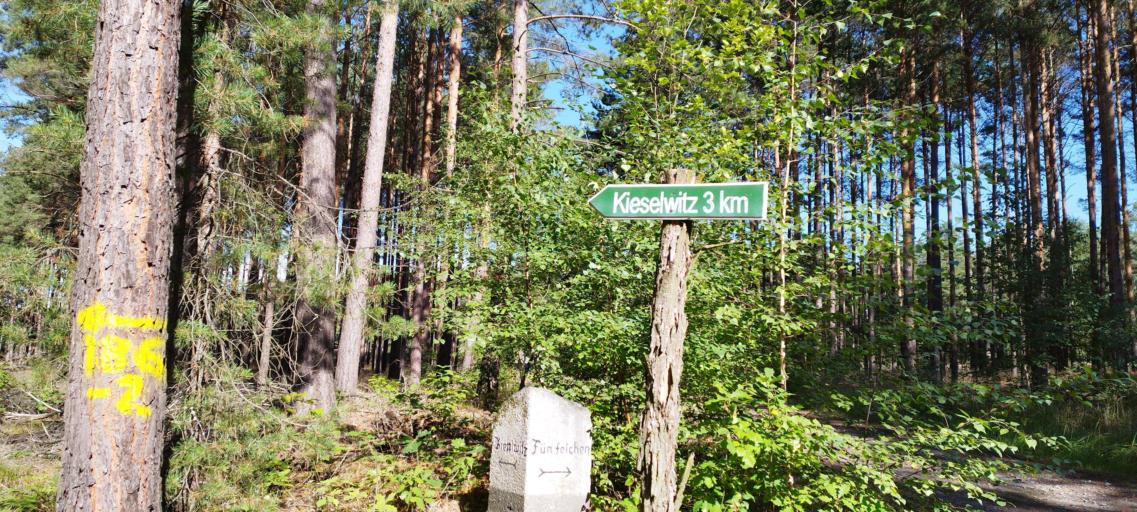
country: DE
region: Brandenburg
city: Lawitz
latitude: 52.1093
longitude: 14.5481
